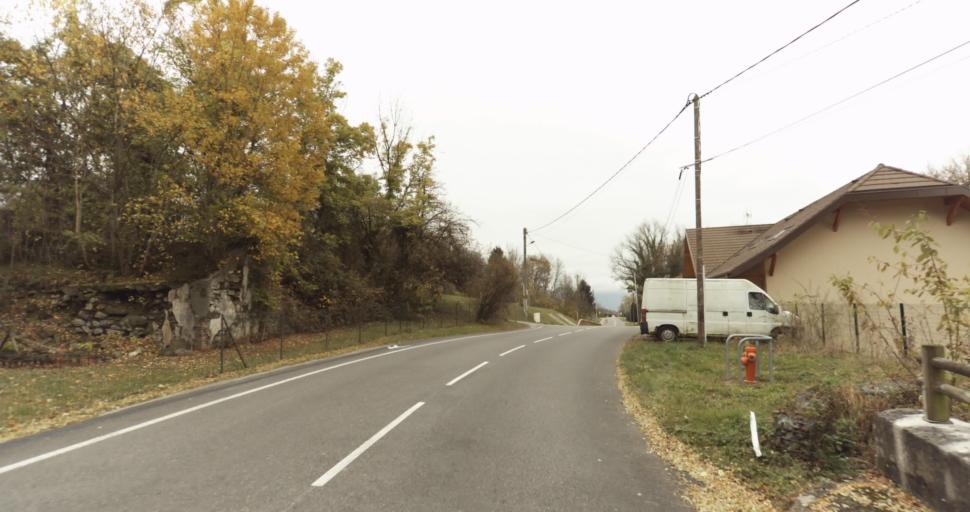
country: FR
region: Rhone-Alpes
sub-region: Departement de la Haute-Savoie
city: Saint-Martin-Bellevue
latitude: 45.9736
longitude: 6.1347
